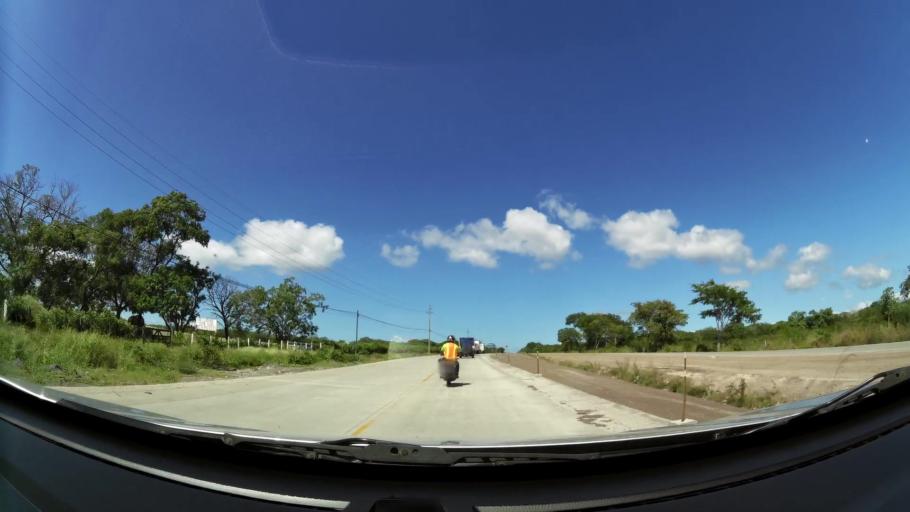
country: CR
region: Guanacaste
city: Bagaces
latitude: 10.5032
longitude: -85.2314
